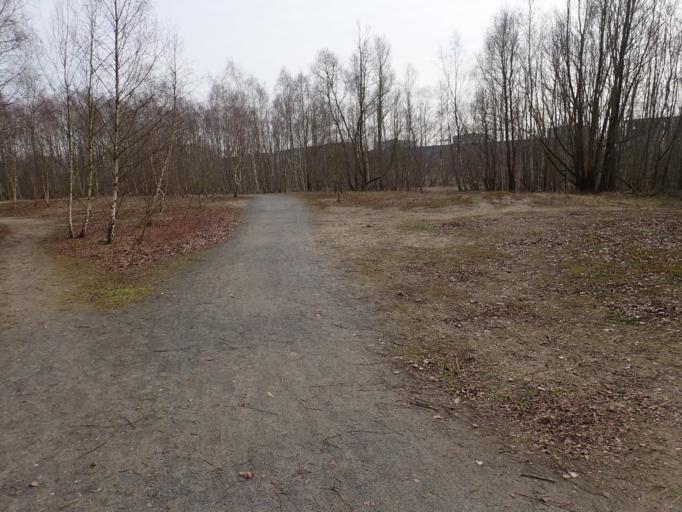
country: BE
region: Flanders
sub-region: Provincie Antwerpen
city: Zwijndrecht
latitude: 51.2221
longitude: 4.3634
